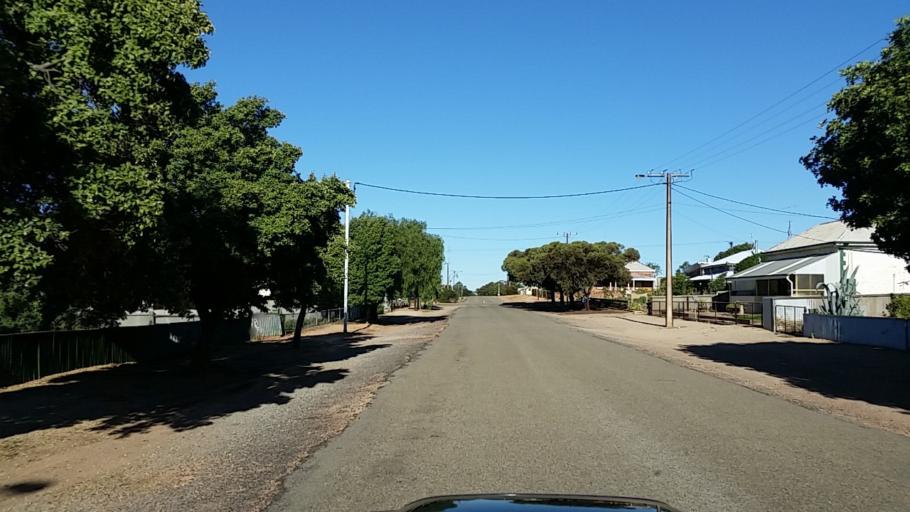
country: AU
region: South Australia
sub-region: Peterborough
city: Peterborough
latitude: -32.9761
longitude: 138.8328
